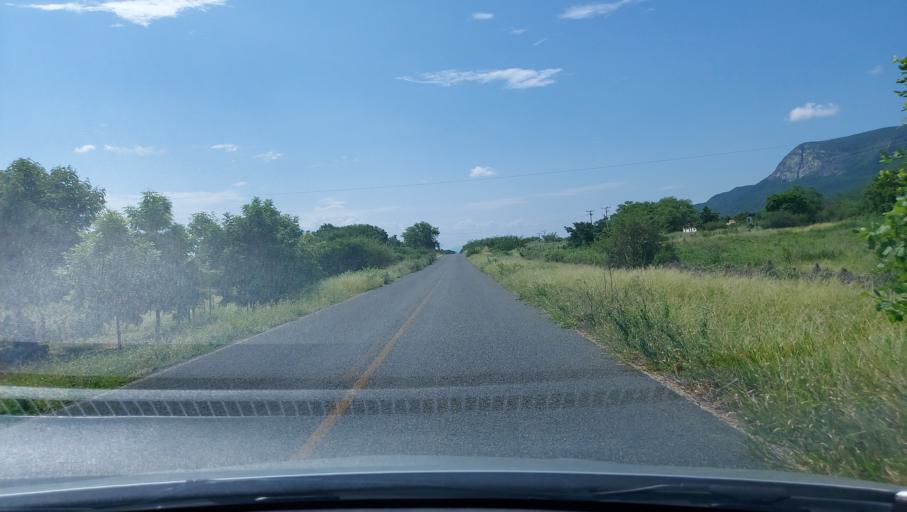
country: BR
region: Bahia
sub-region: Oliveira Dos Brejinhos
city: Beira Rio
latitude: -12.1458
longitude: -42.5557
